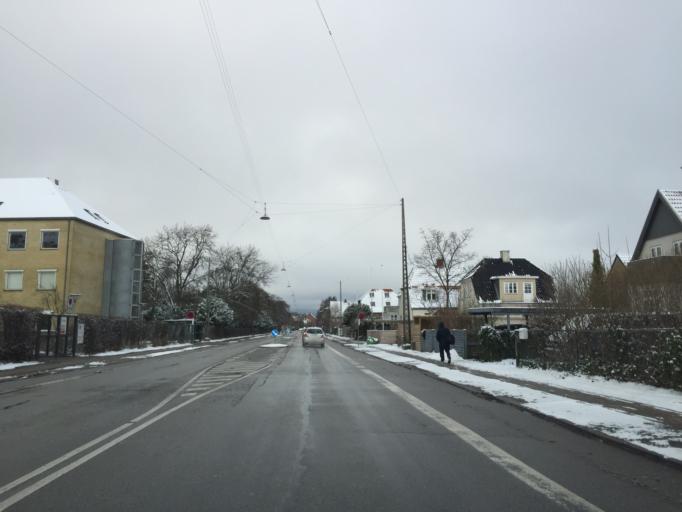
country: DK
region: Capital Region
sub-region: Kobenhavn
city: Christianshavn
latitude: 55.6555
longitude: 12.6223
